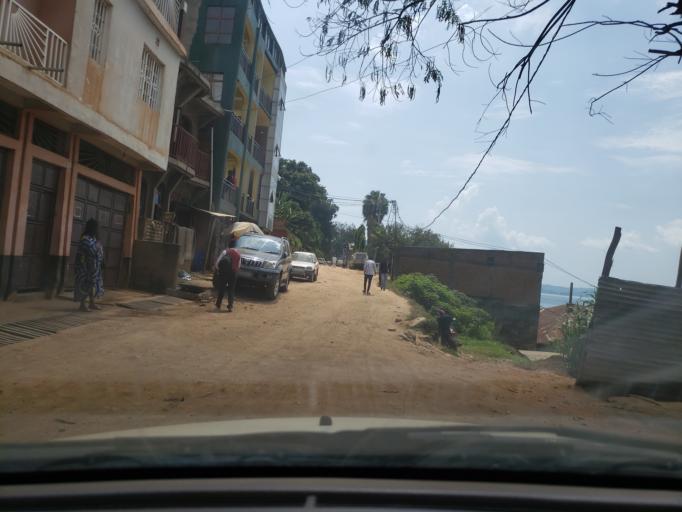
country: CD
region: South Kivu
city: Bukavu
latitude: -2.4975
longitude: 28.8619
